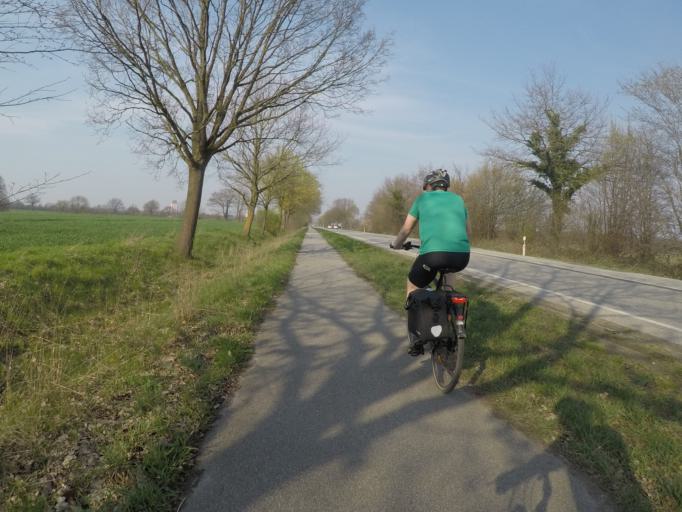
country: DE
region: Schleswig-Holstein
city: Gross Niendorf
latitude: 53.8575
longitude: 10.2463
